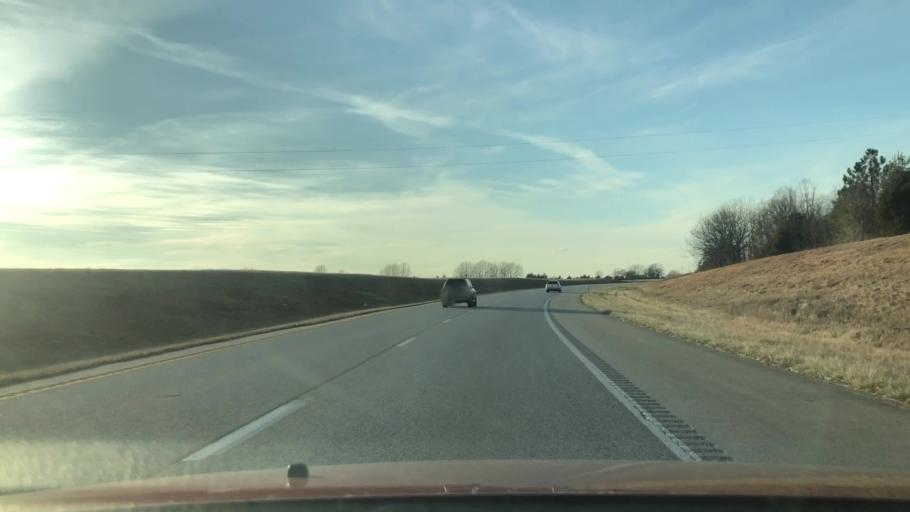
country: US
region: Missouri
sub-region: Webster County
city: Seymour
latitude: 37.1188
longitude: -92.6903
